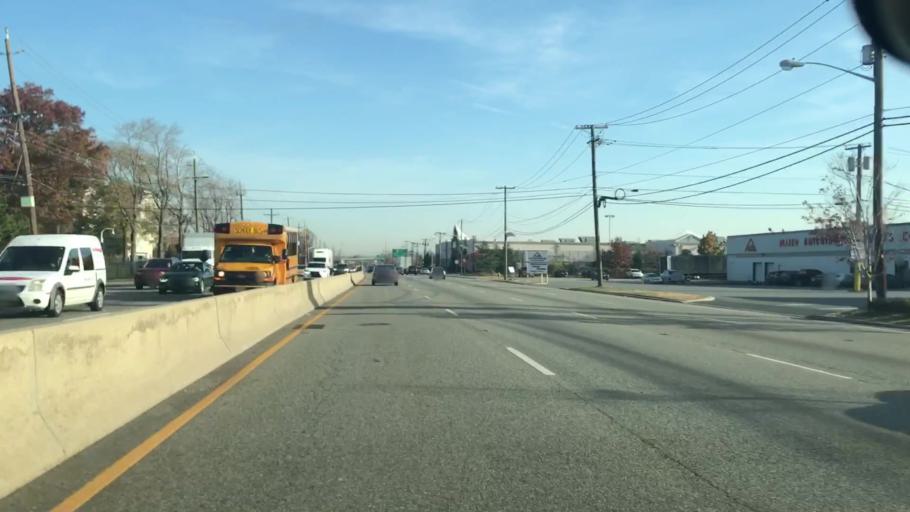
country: US
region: New Jersey
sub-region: Bergen County
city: East Rutherford
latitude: 40.8268
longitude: -74.0949
